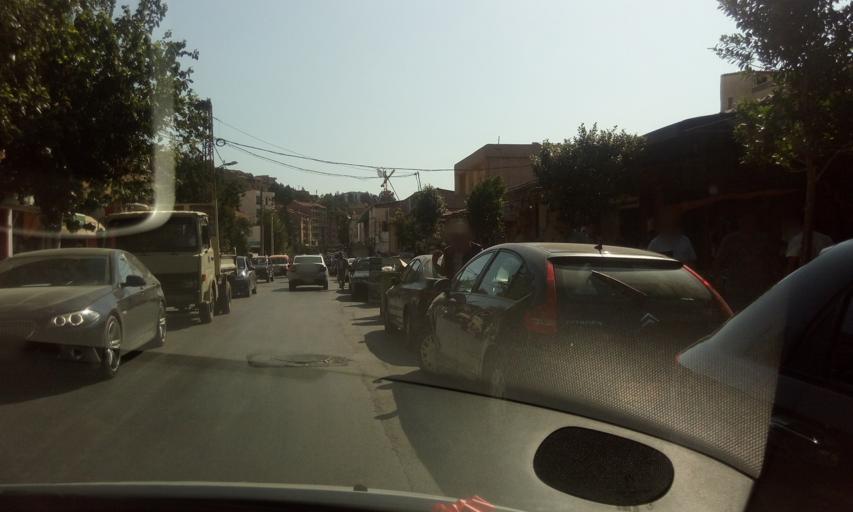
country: DZ
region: Bejaia
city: Seddouk
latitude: 36.6122
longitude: 4.6889
